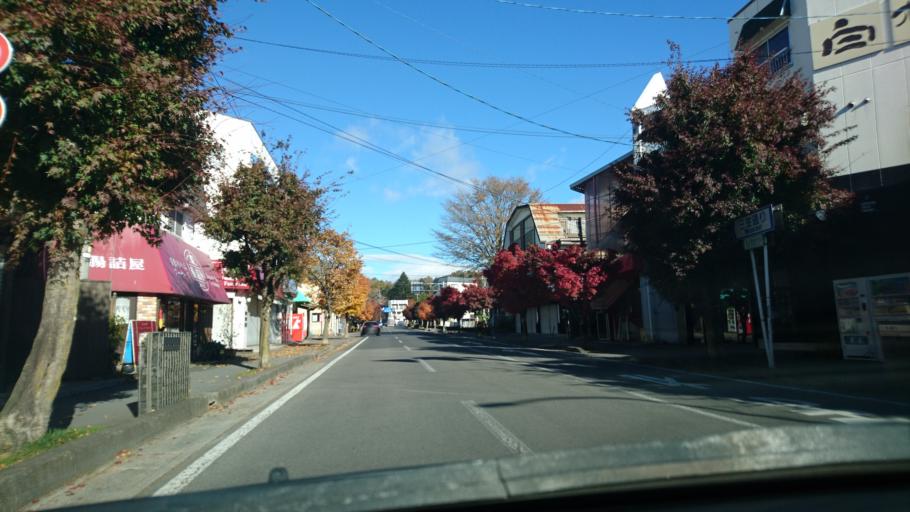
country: JP
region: Nagano
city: Komoro
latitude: 36.3573
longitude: 138.6341
